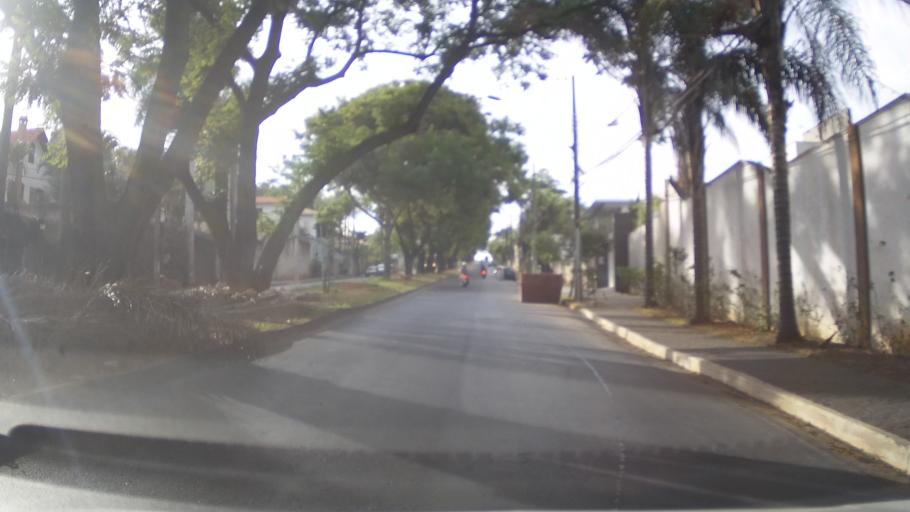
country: BR
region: Minas Gerais
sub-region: Belo Horizonte
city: Belo Horizonte
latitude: -19.8624
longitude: -43.9917
